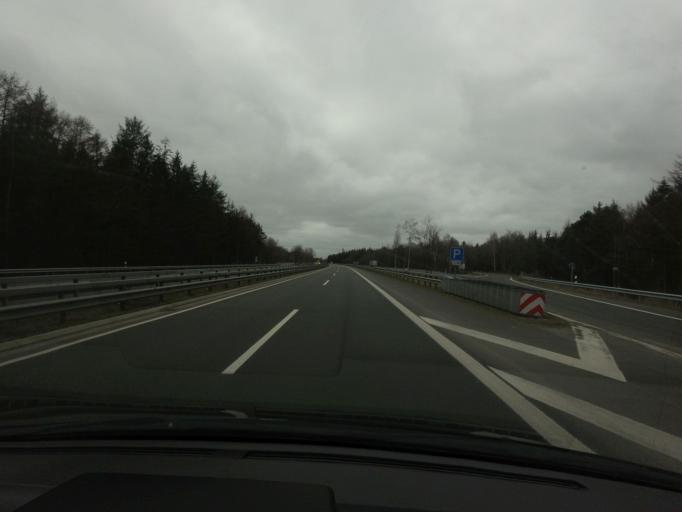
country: DE
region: Lower Saxony
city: Bad Zwischenahn
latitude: 53.2468
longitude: 8.0111
